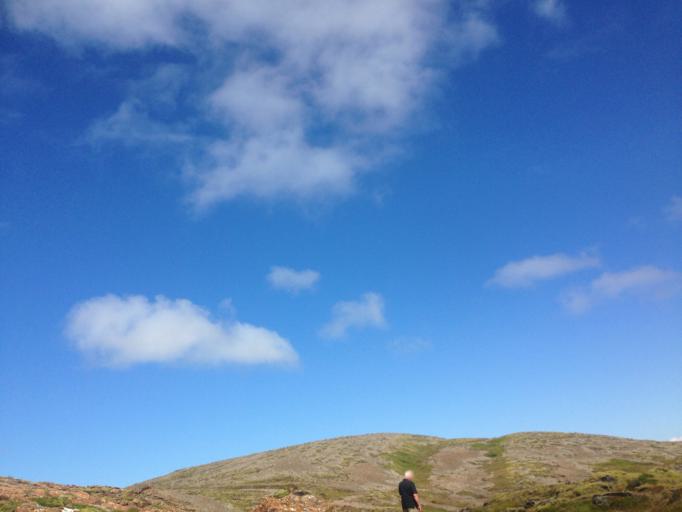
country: IS
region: Capital Region
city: Alftanes
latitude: 63.9536
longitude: -22.0800
